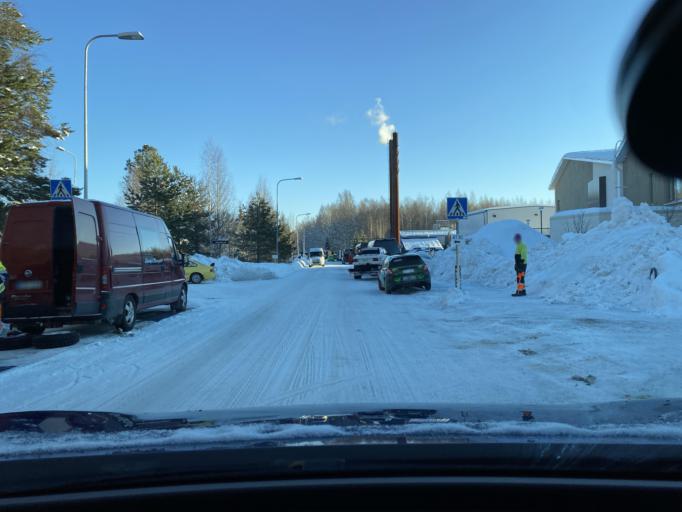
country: FI
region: Southern Savonia
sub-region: Mikkeli
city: Kangasniemi
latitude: 61.9869
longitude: 26.6372
